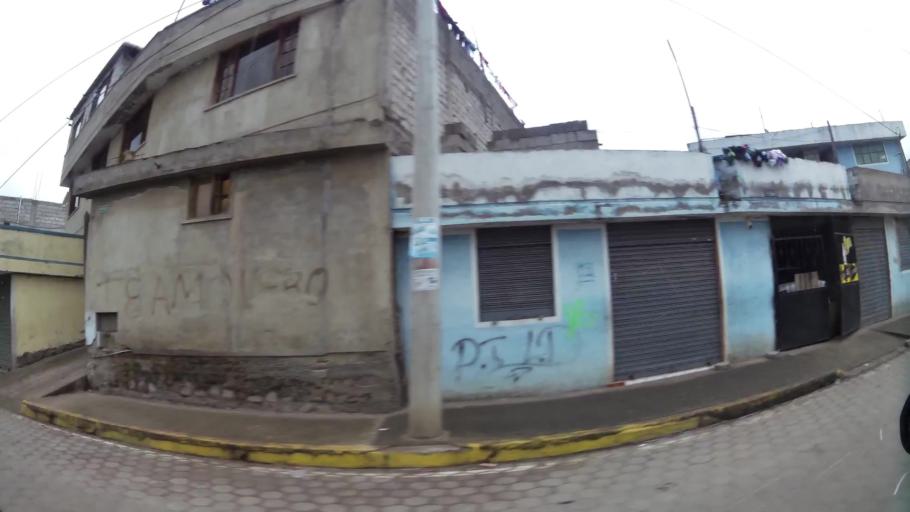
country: EC
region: Pichincha
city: Sangolqui
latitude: -0.3204
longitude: -78.5334
